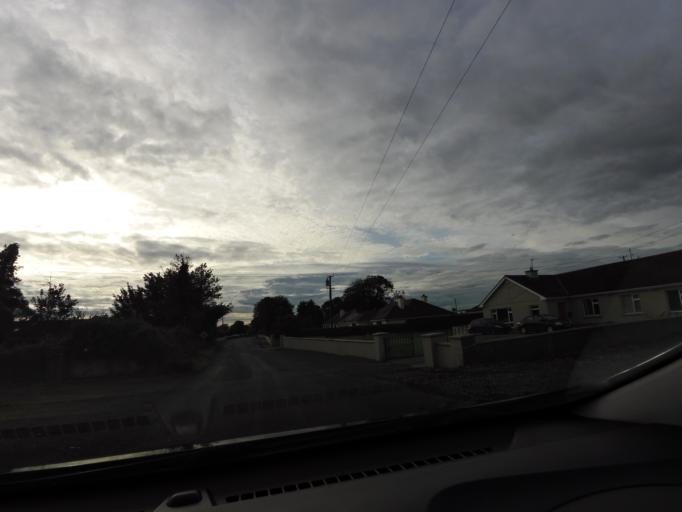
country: IE
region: Connaught
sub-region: County Galway
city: Ballinasloe
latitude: 53.3596
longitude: -8.2176
